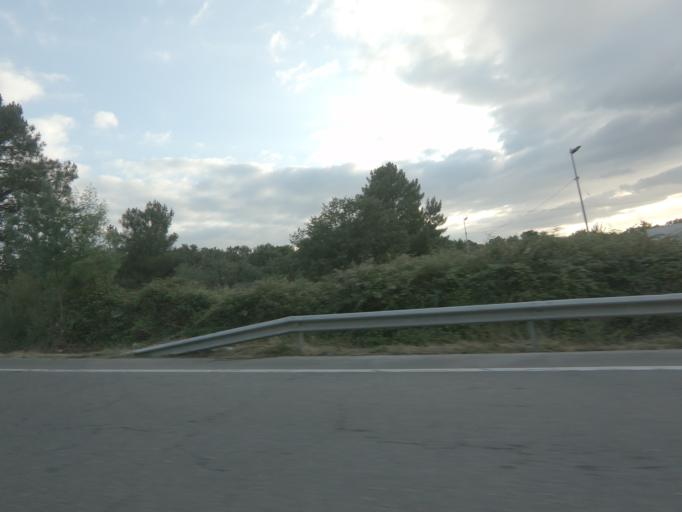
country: ES
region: Galicia
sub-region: Provincia de Ourense
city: Taboadela
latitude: 42.2775
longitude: -7.8363
